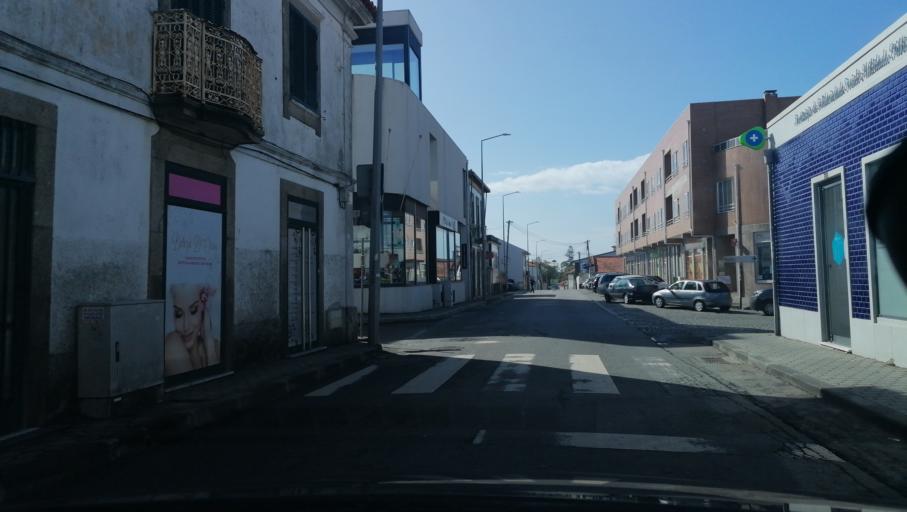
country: PT
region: Porto
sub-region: Vila Nova de Gaia
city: Sao Felix da Marinha
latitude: 41.0474
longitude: -8.6284
